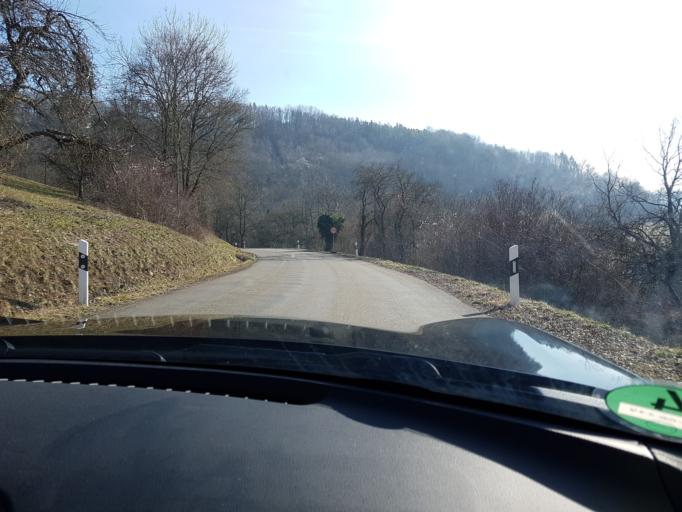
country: DE
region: Baden-Wuerttemberg
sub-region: Regierungsbezirk Stuttgart
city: Langenburg
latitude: 49.2485
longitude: 9.8558
